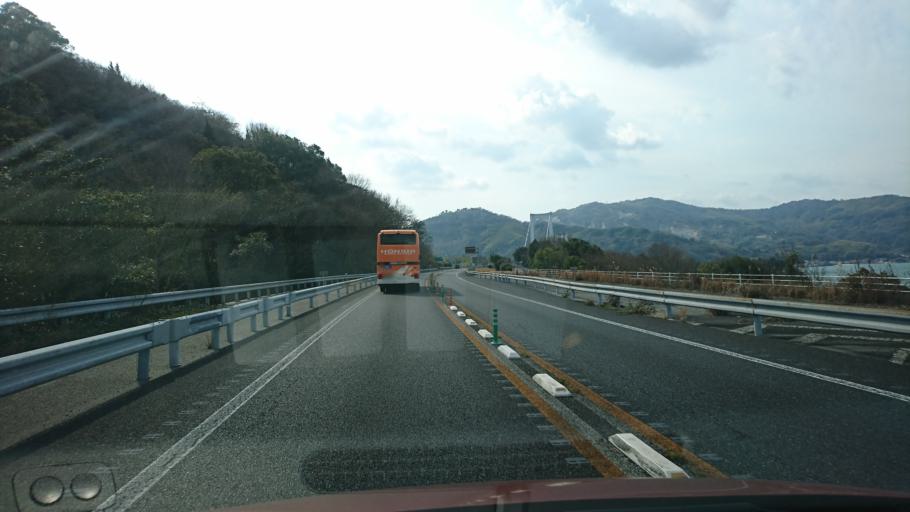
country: JP
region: Hiroshima
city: Innoshima
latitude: 34.1997
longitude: 133.0786
